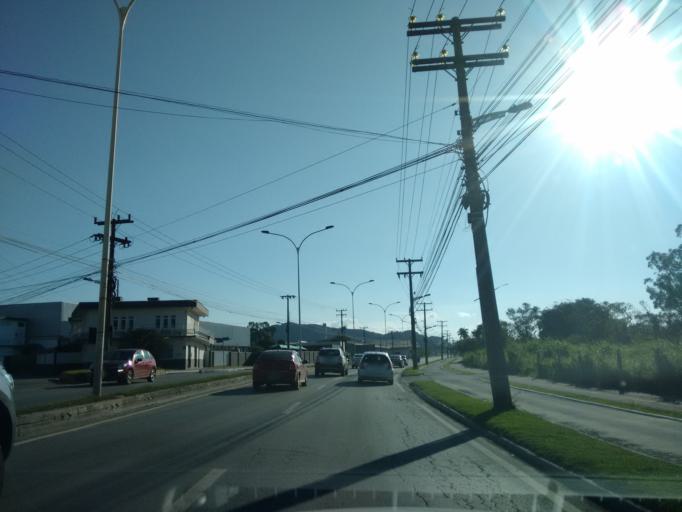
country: BR
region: Santa Catarina
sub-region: Itajai
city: Itajai
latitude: -26.8914
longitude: -48.7155
